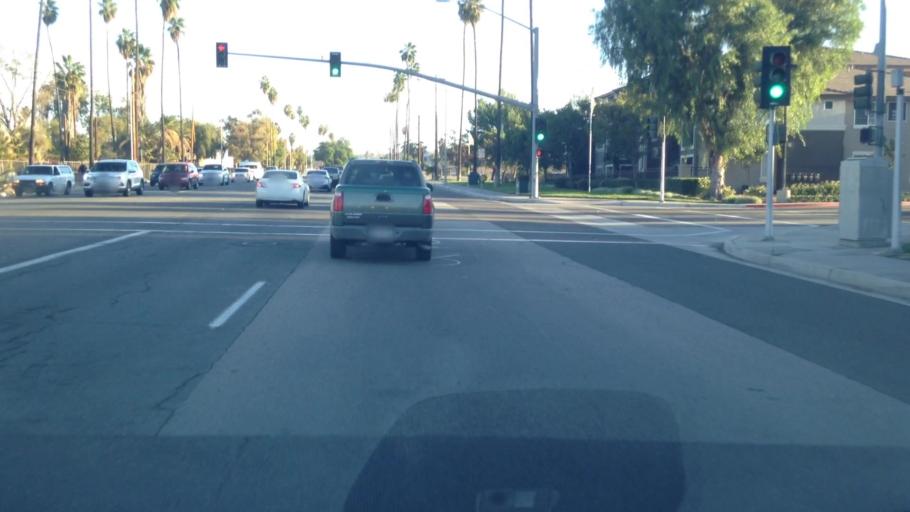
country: US
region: California
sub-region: Riverside County
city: Riverside
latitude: 33.9113
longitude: -117.4393
